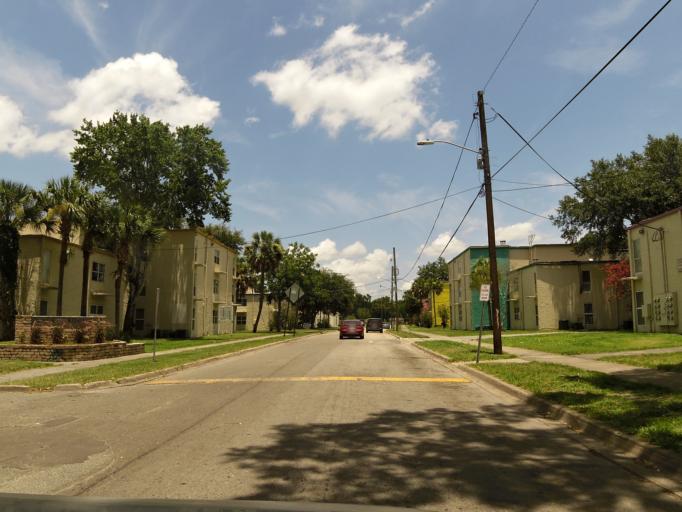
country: US
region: Florida
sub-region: Duval County
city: Jacksonville
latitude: 30.3493
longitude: -81.6954
